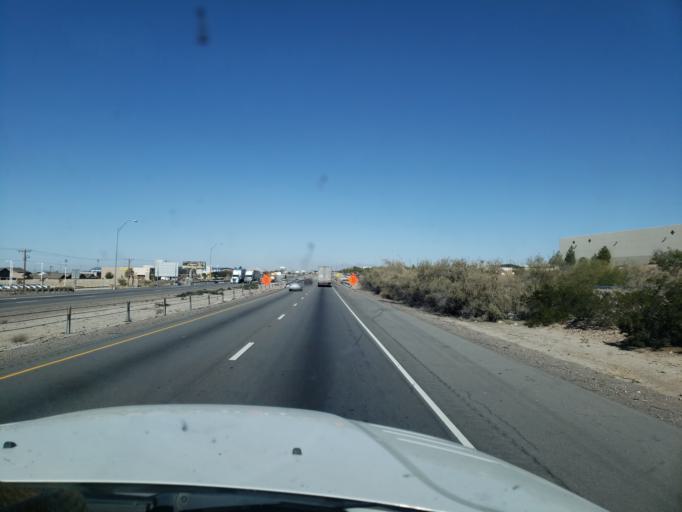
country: US
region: Texas
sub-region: El Paso County
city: Canutillo
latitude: 31.8897
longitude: -106.5827
